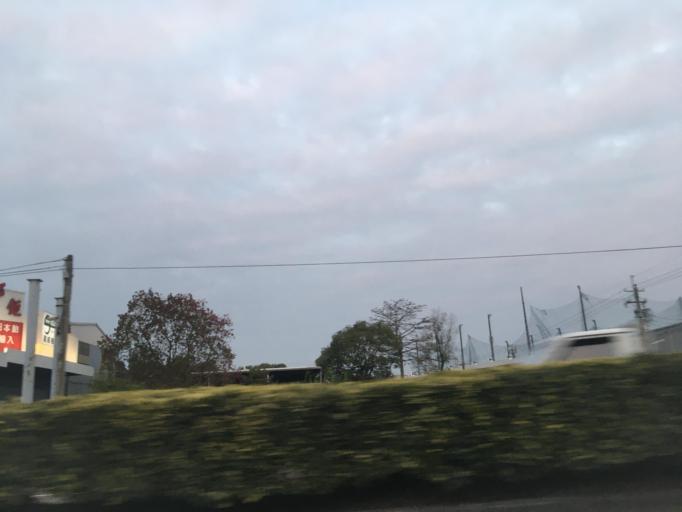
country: TW
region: Taiwan
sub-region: Yunlin
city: Douliu
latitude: 23.6960
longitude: 120.4617
